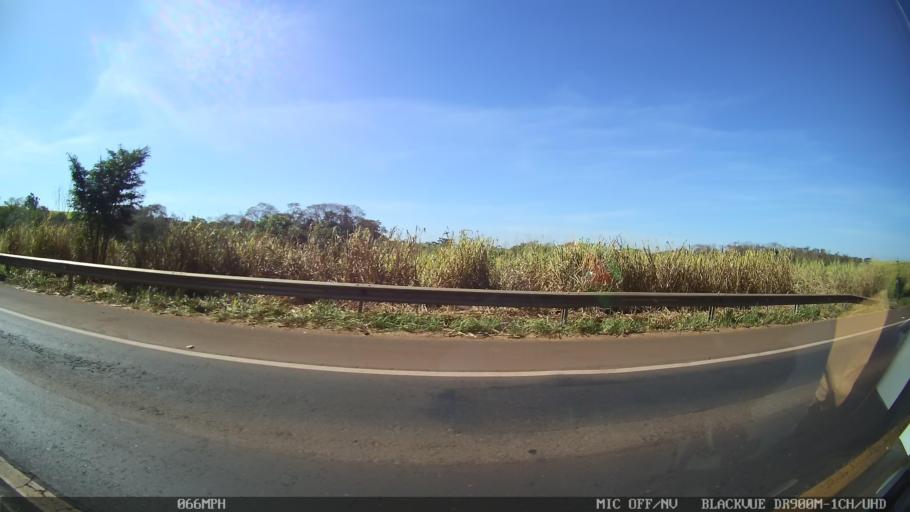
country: BR
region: Sao Paulo
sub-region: Olimpia
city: Olimpia
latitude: -20.7049
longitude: -48.8853
